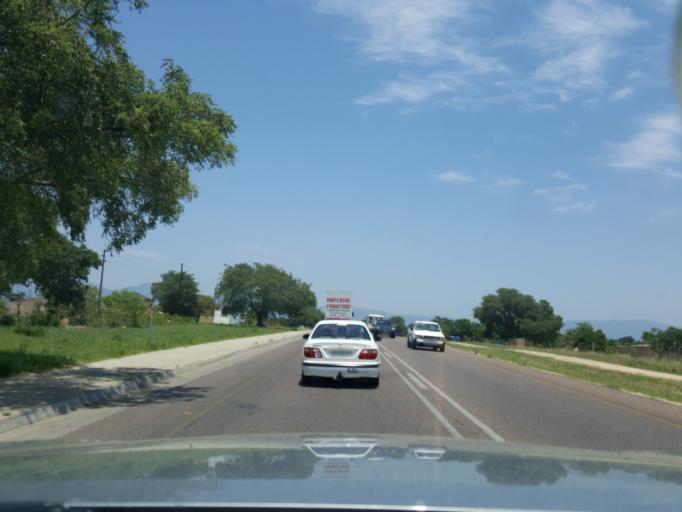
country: ZA
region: Limpopo
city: Thulamahashi
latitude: -24.7850
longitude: 31.0751
